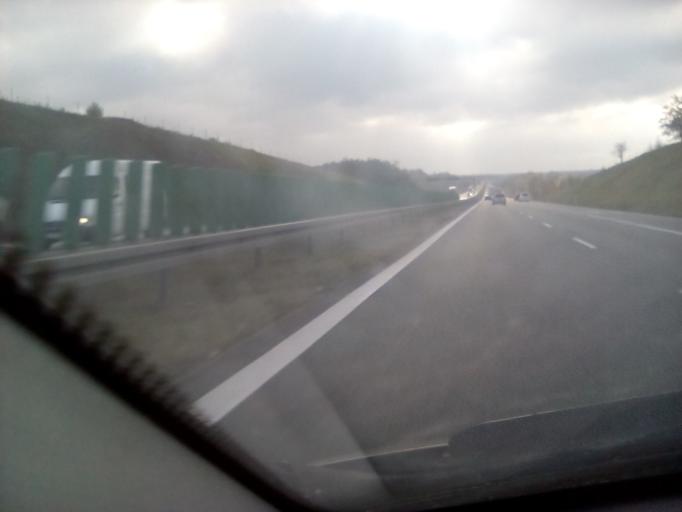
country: PL
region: Masovian Voivodeship
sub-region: Powiat bialobrzeski
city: Promna
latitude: 51.6743
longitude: 20.9458
